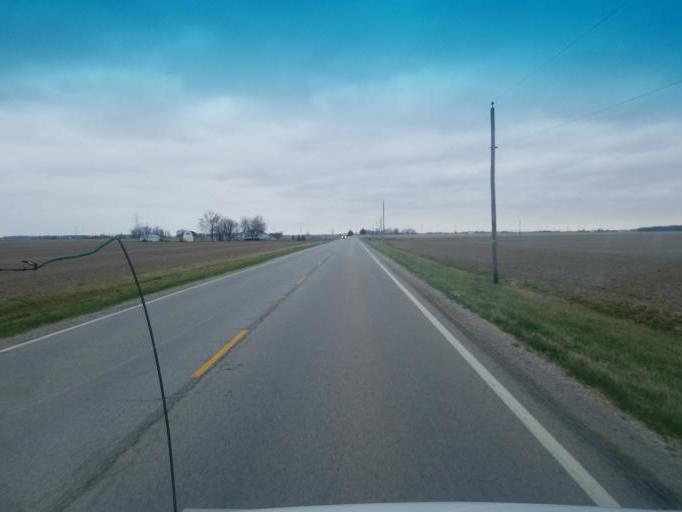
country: US
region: Ohio
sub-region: Allen County
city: Delphos
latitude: 40.9320
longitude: -84.4477
